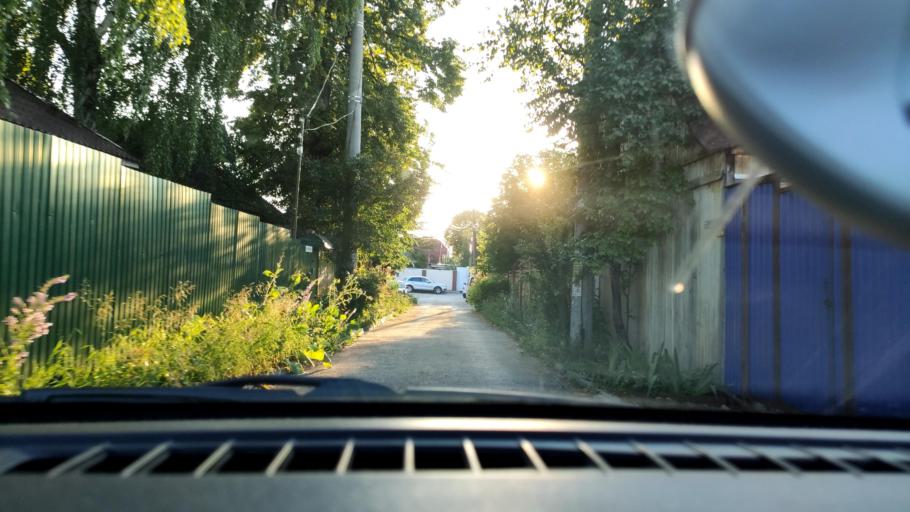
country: RU
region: Samara
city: Samara
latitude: 53.2609
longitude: 50.1920
